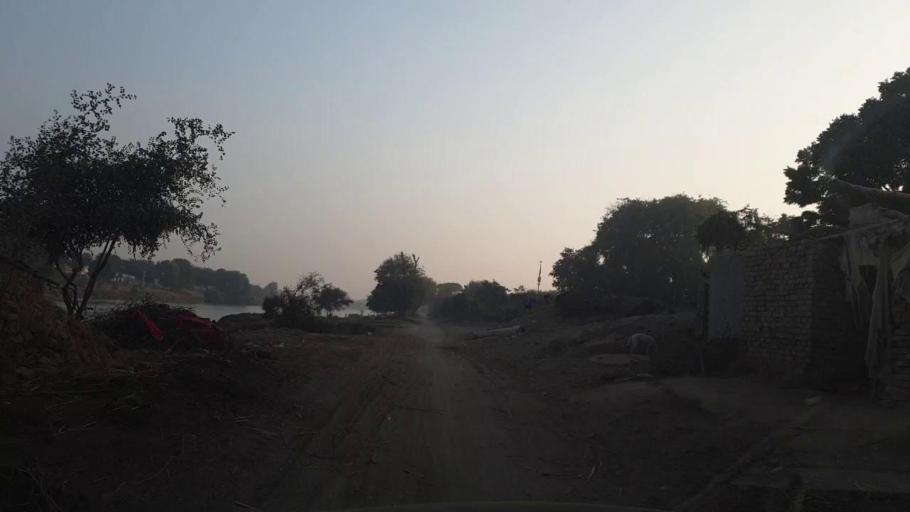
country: PK
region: Sindh
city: Ubauro
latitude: 28.3102
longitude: 69.7898
